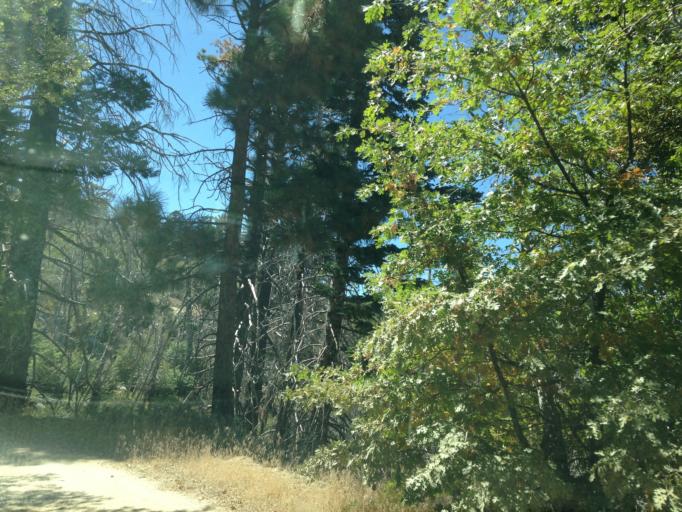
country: US
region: California
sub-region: San Bernardino County
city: Running Springs
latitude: 34.2495
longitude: -117.0741
